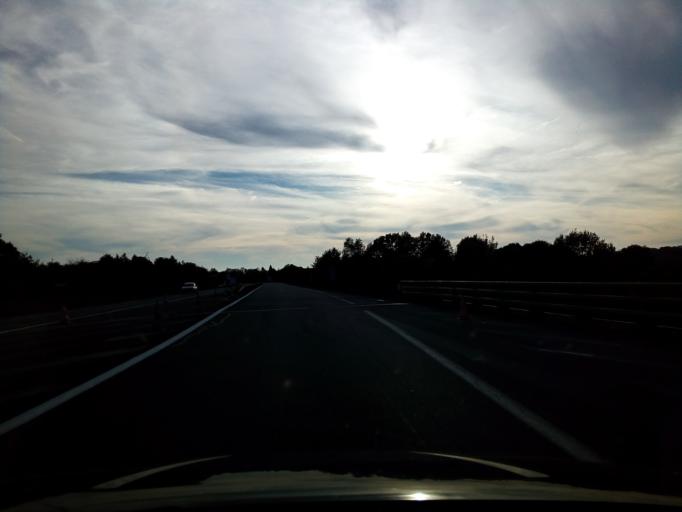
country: FR
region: Poitou-Charentes
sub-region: Departement de la Charente
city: Chasseneuil-sur-Bonnieure
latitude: 45.8267
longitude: 0.4610
